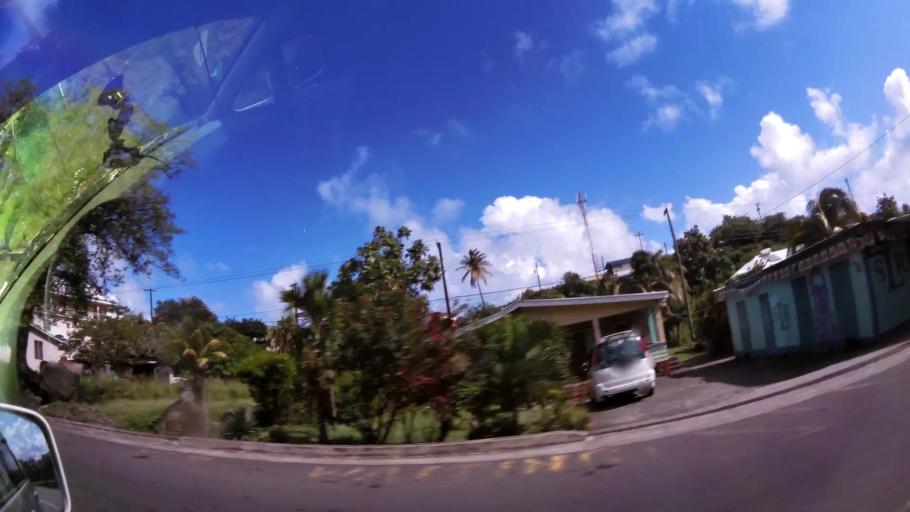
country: VC
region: Saint George
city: Kingstown
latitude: 13.1333
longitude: -61.1839
